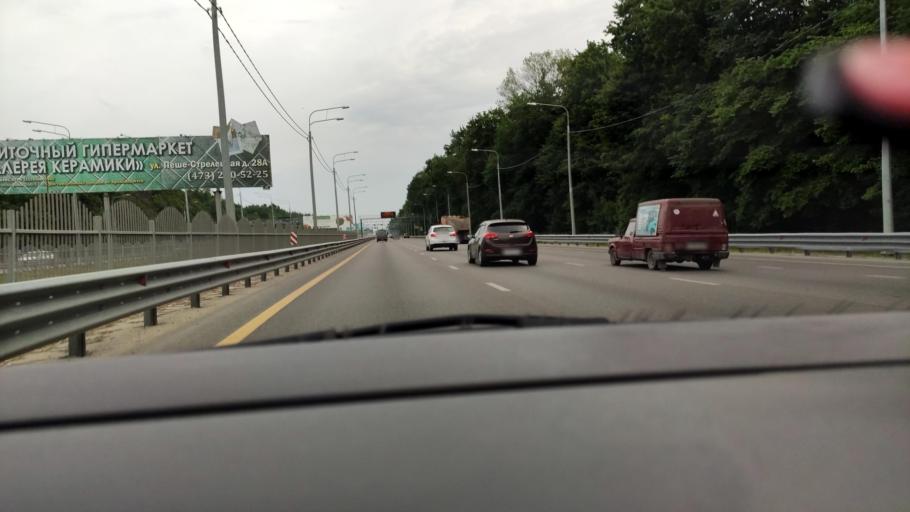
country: RU
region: Voronezj
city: Podgornoye
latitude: 51.7554
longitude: 39.1890
